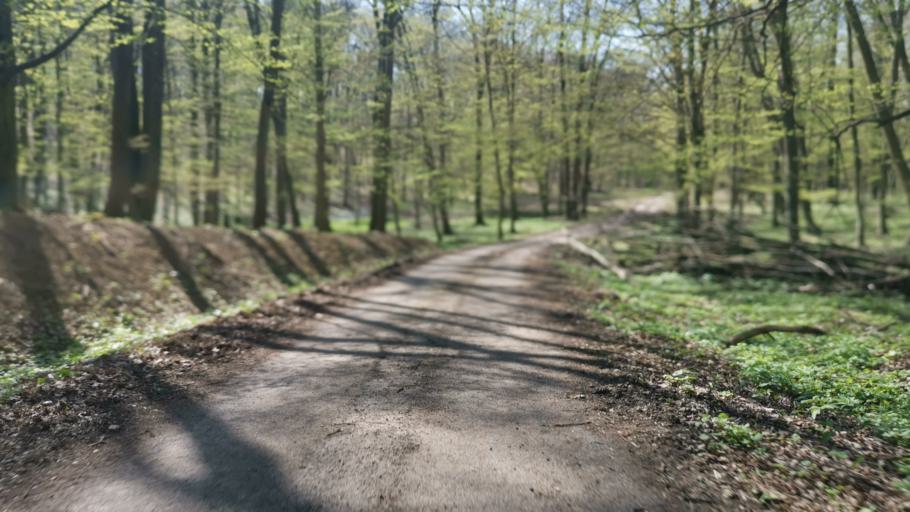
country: SK
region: Trnavsky
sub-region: Okres Skalica
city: Skalica
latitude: 48.7362
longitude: 17.2460
